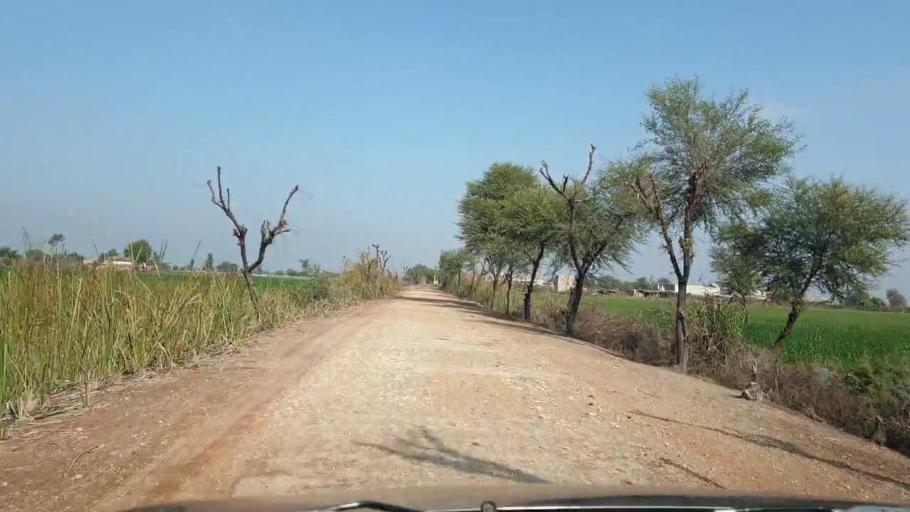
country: PK
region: Sindh
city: Sinjhoro
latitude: 26.0658
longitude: 68.7725
